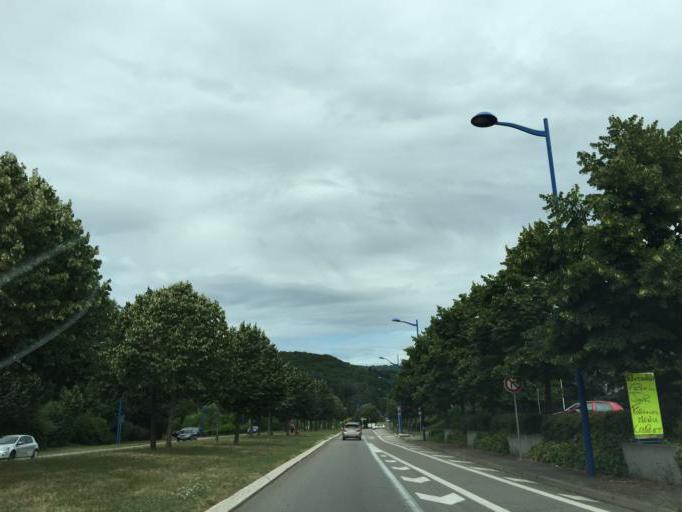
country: FR
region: Rhone-Alpes
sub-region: Departement de la Loire
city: Unieux
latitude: 45.3945
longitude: 4.2649
